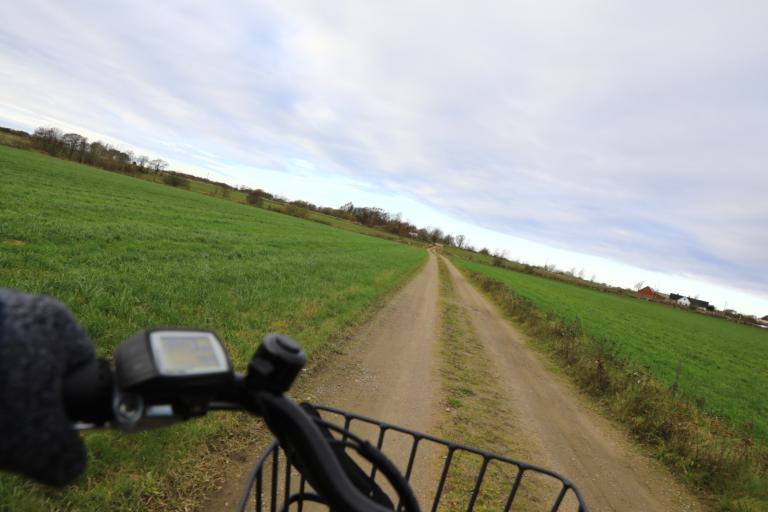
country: SE
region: Halland
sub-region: Varbergs Kommun
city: Traslovslage
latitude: 57.0593
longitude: 12.3274
